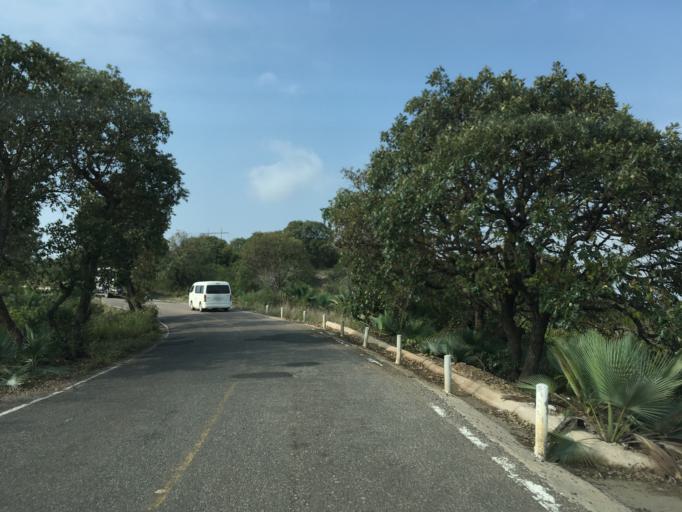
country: MX
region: Oaxaca
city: Magdalena Zahuatlan
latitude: 17.3664
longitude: -97.2158
